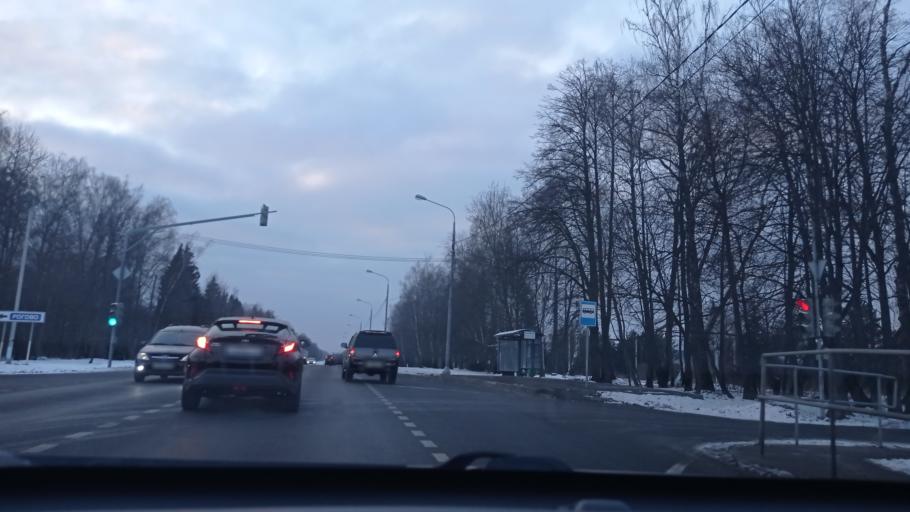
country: RU
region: Moskovskaya
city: Kievskij
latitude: 55.2367
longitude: 37.0372
